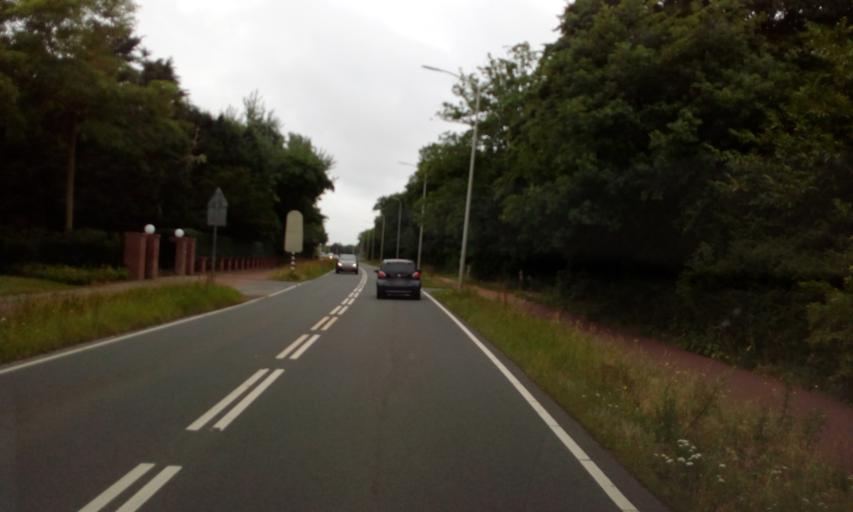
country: NL
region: South Holland
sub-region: Gemeente Westland
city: Poeldijk
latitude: 52.0459
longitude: 4.2084
